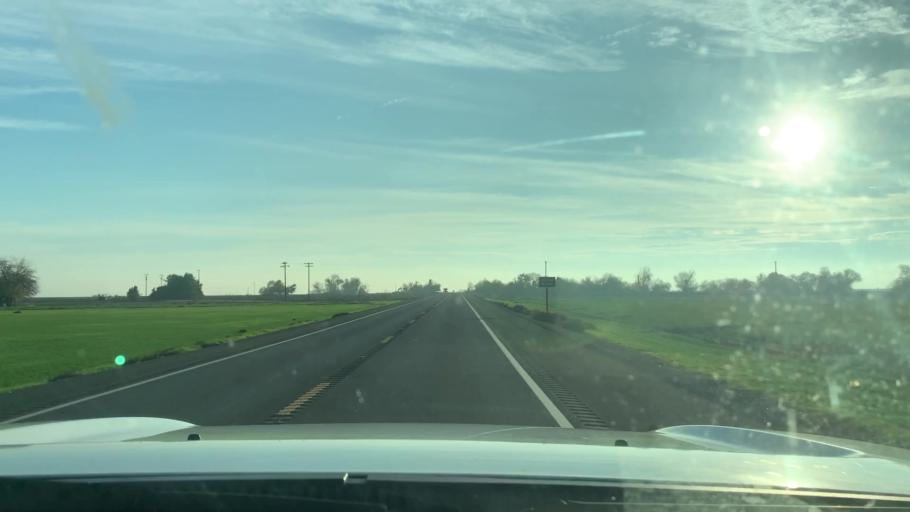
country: US
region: California
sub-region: Kings County
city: Stratford
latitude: 36.1836
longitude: -119.8324
